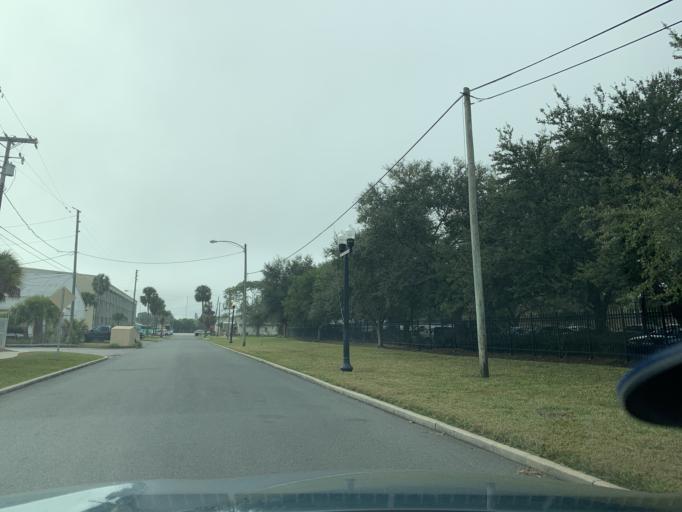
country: US
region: Florida
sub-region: Pinellas County
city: Saint Petersburg
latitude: 27.7578
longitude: -82.6354
